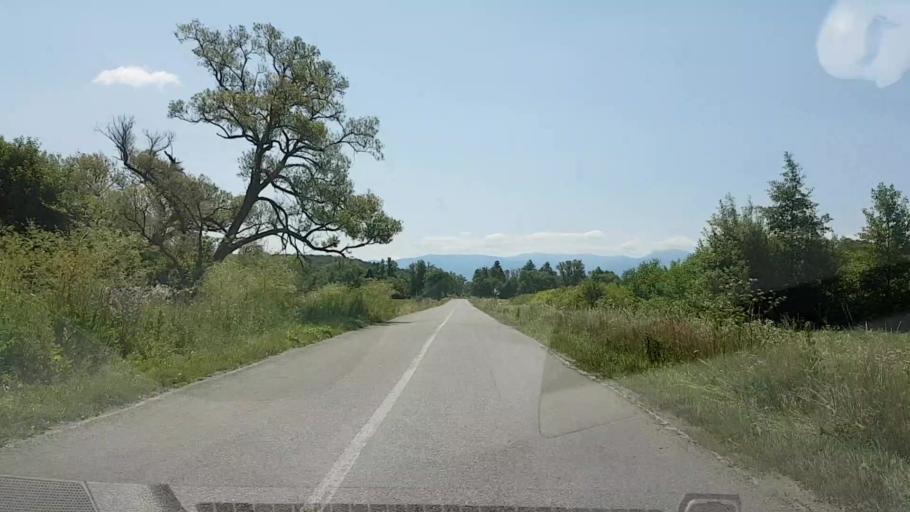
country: RO
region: Brasov
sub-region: Comuna Voila
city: Voila
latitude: 45.8612
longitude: 24.8257
